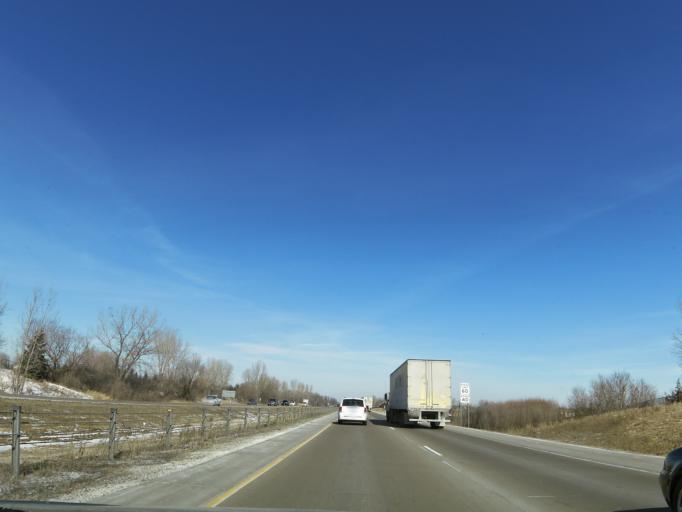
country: US
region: Minnesota
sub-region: Ramsey County
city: North Saint Paul
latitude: 45.0073
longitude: -92.9577
